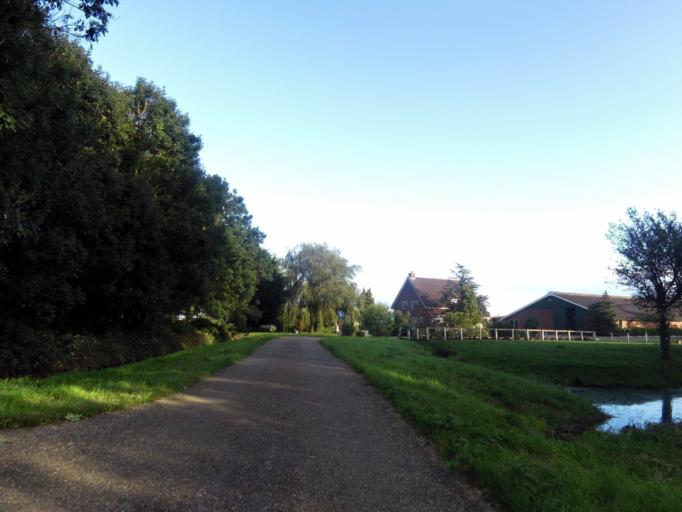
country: NL
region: South Holland
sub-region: Gemeente Alphen aan den Rijn
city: Alphen aan den Rijn
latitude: 52.1144
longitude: 4.6094
